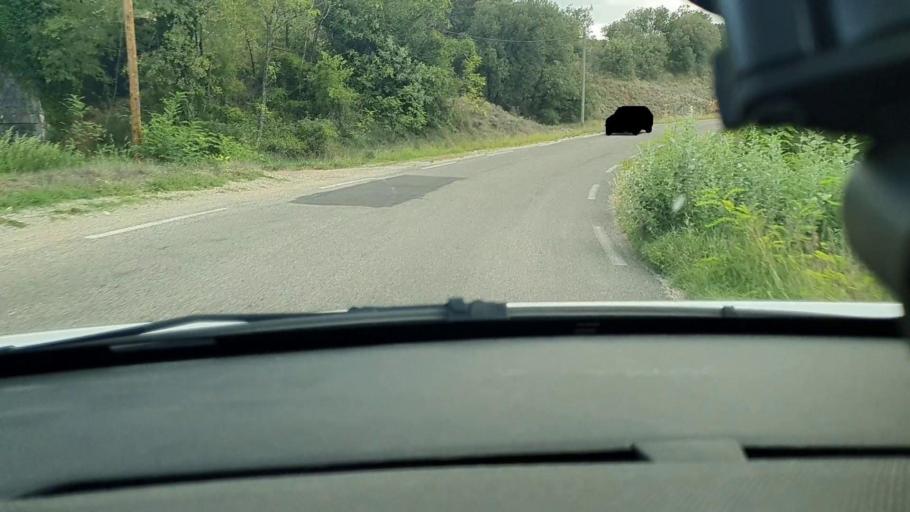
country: FR
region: Languedoc-Roussillon
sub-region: Departement du Gard
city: Les Mages
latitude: 44.2213
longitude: 4.1743
